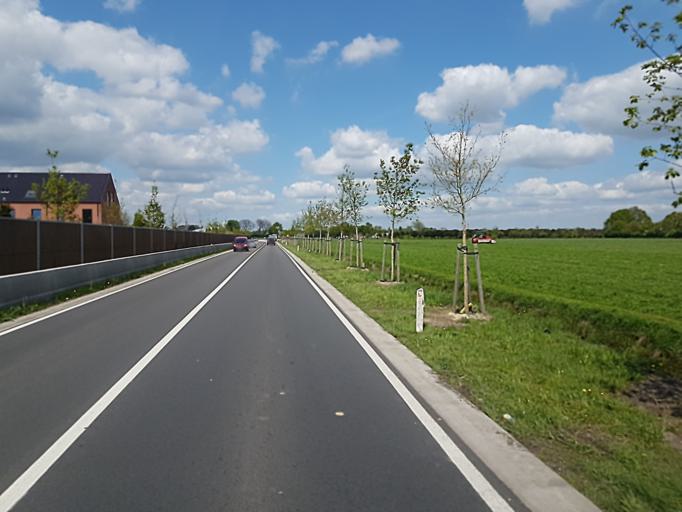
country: BE
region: Flanders
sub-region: Provincie Antwerpen
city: Brecht
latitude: 51.3540
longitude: 4.6496
